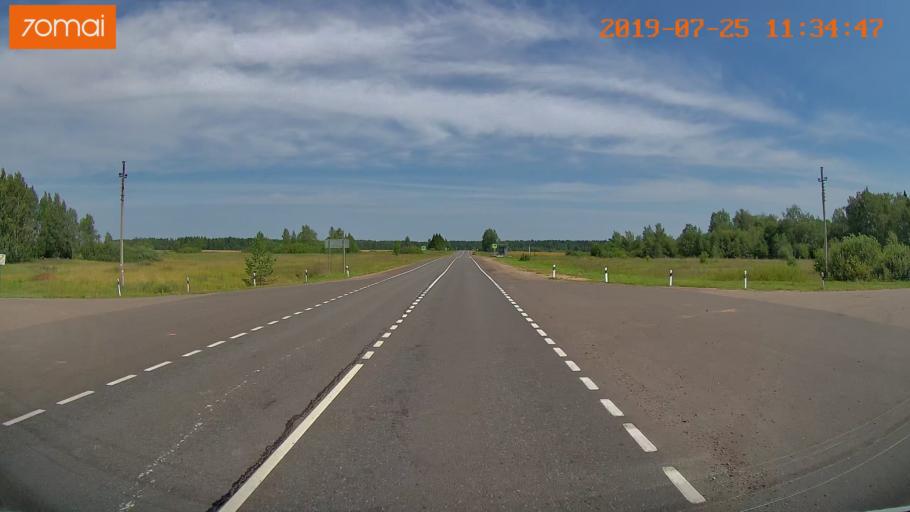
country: RU
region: Ivanovo
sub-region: Privolzhskiy Rayon
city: Ples
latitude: 57.4035
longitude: 41.4187
